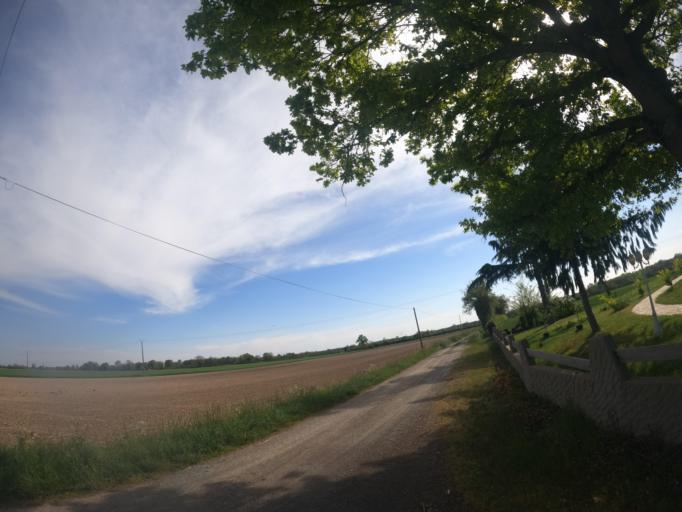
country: FR
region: Poitou-Charentes
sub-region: Departement des Deux-Sevres
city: Saint-Varent
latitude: 46.9243
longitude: -0.2398
